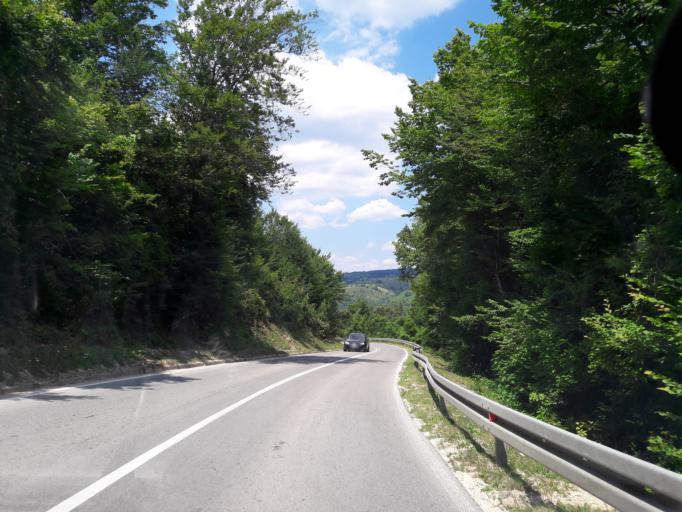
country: BA
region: Republika Srpska
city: Sipovo
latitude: 44.1969
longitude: 17.1532
